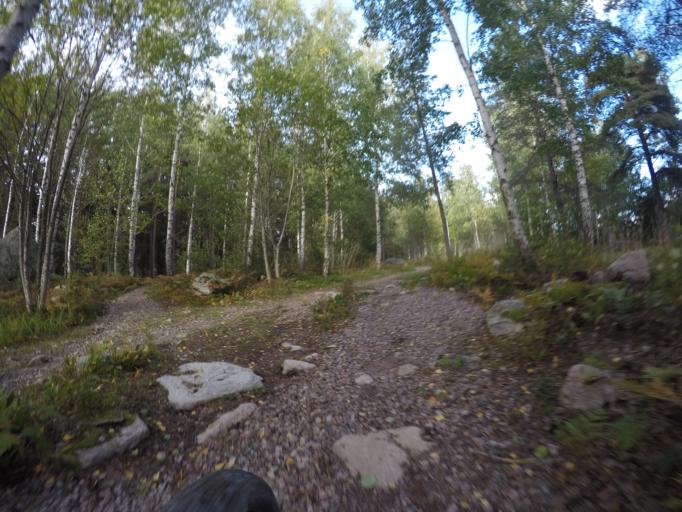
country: SE
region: Vaestmanland
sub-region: Kopings Kommun
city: Koping
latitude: 59.5269
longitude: 15.9997
